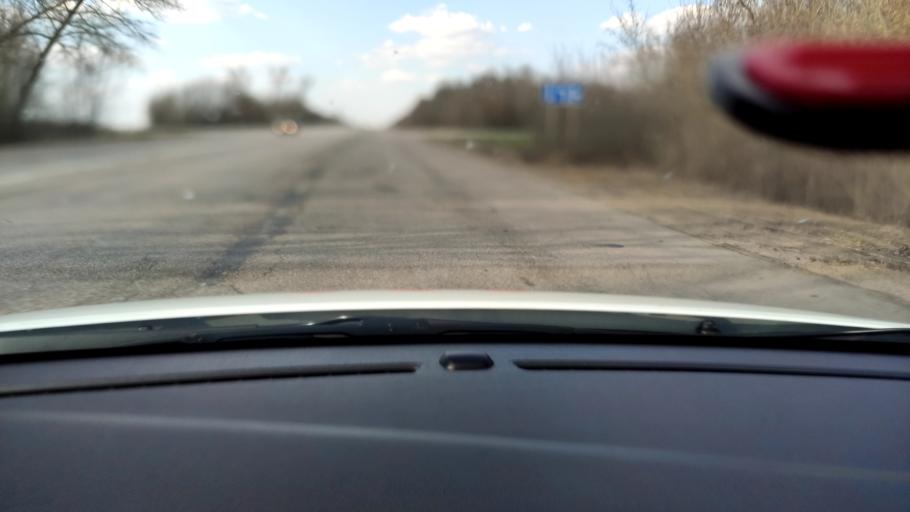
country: RU
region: Voronezj
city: Uryv-Pokrovka
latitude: 51.2289
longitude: 39.0602
